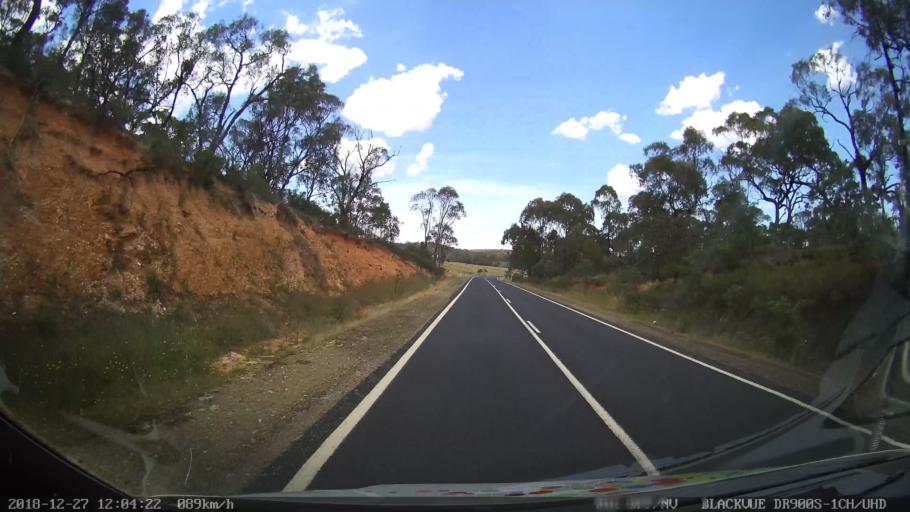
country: AU
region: New South Wales
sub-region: Blayney
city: Blayney
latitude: -33.7964
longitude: 149.3511
